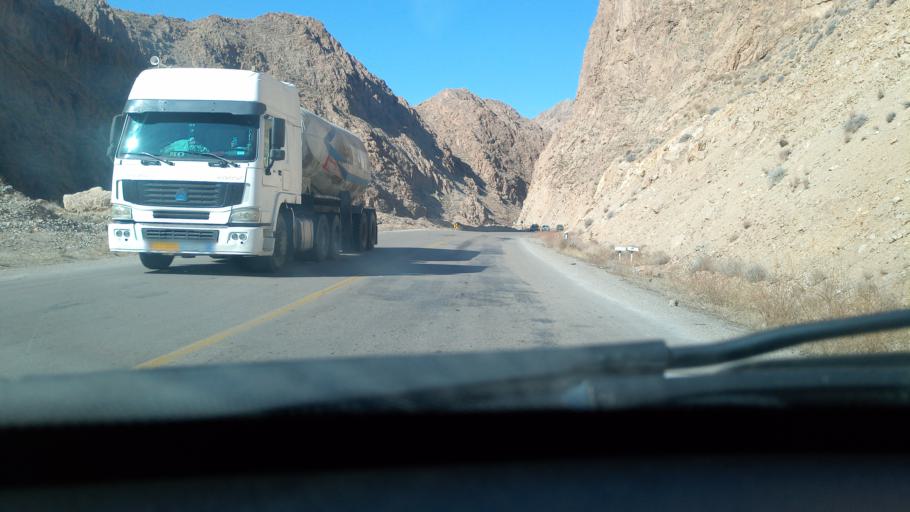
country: IR
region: Khorasan-e Shomali
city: Esfarayen
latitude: 37.1706
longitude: 57.4262
